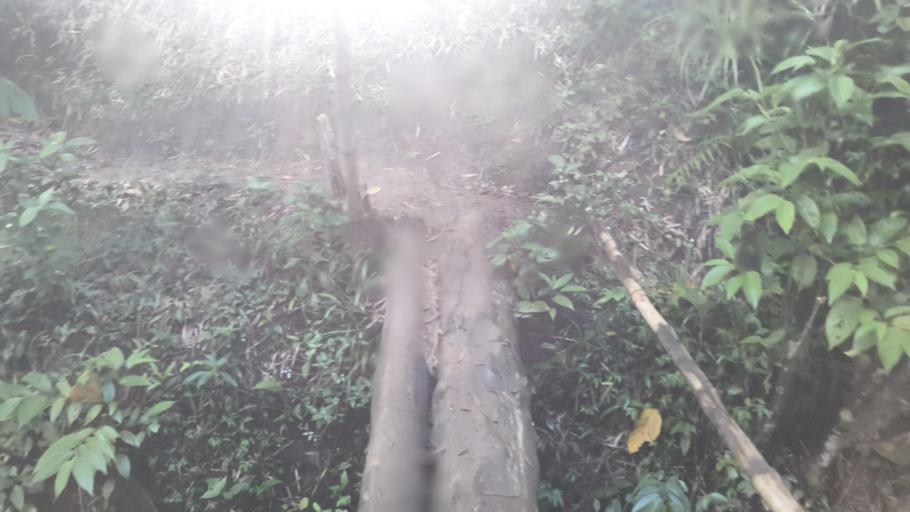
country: PG
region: Western Highlands
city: Rauna
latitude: -5.8022
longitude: 144.3680
